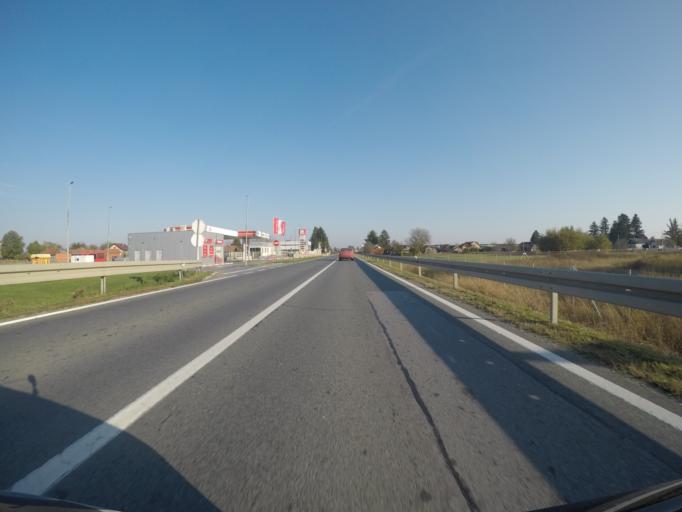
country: HR
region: Virovitick-Podravska
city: Pitomaca
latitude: 45.9676
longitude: 17.2000
